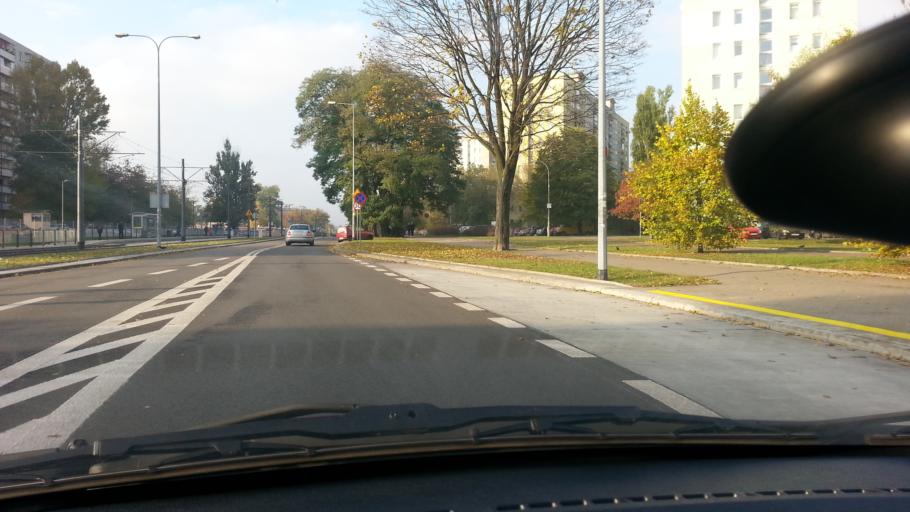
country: PL
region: Masovian Voivodeship
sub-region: Warszawa
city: Targowek
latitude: 52.2835
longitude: 21.0342
